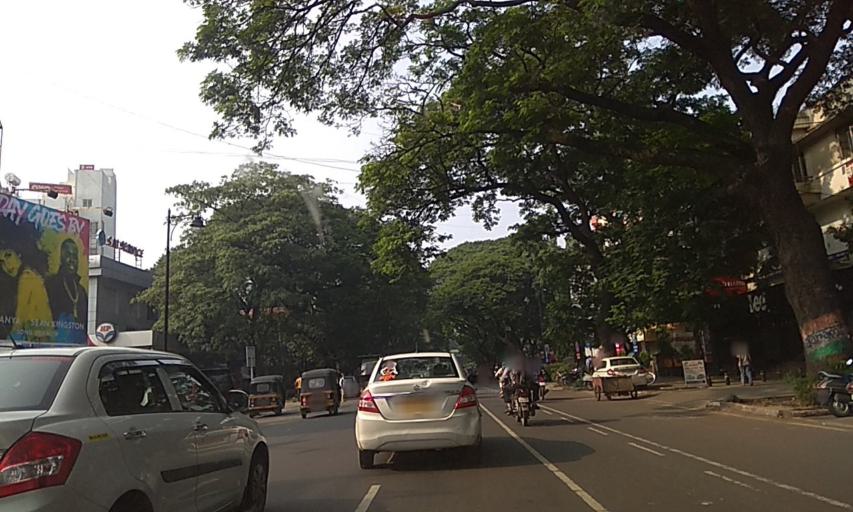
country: IN
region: Maharashtra
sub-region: Pune Division
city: Pune
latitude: 18.5193
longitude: 73.8451
